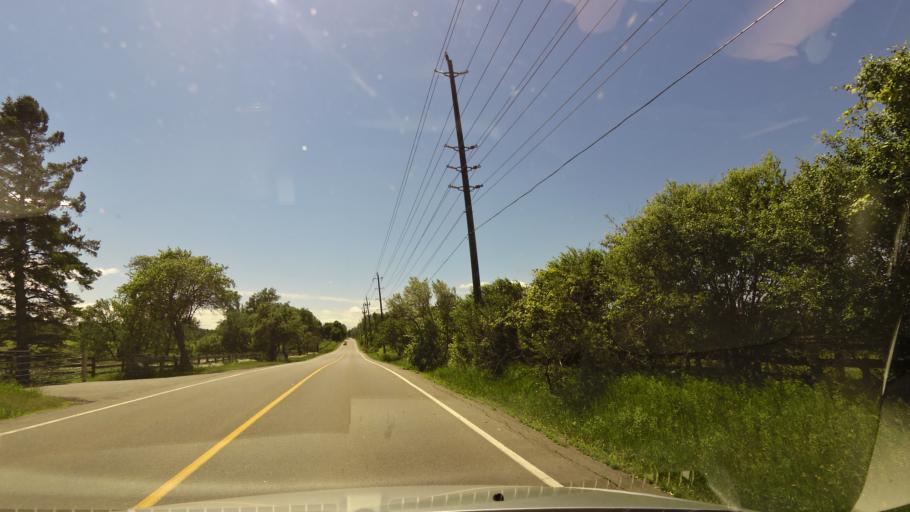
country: CA
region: Ontario
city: Newmarket
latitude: 43.9504
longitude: -79.5173
